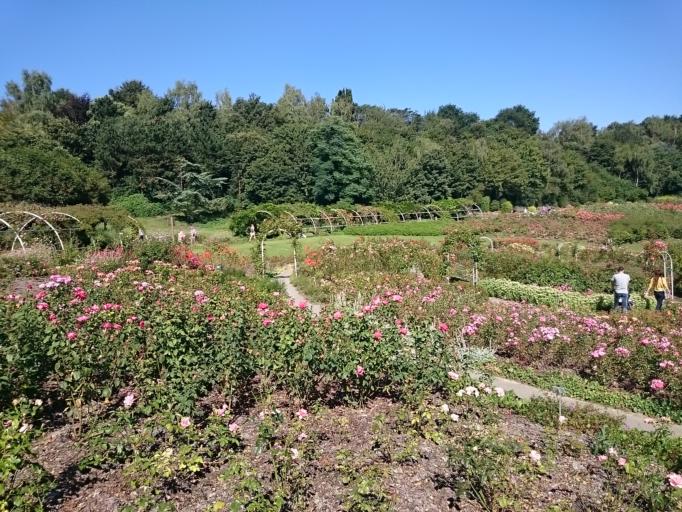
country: FR
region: Lower Normandy
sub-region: Departement du Calvados
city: Saint-Germain-la-Blanche-Herbe
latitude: 49.1980
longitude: -0.3947
